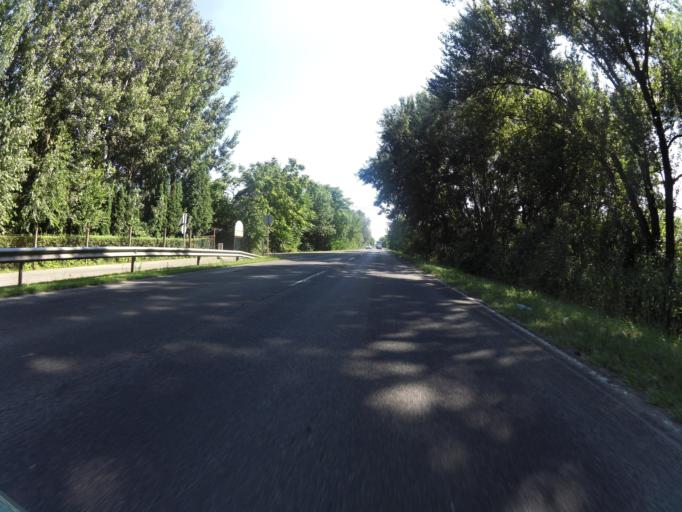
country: HU
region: Csongrad
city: Szatymaz
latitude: 46.3305
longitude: 20.0643
